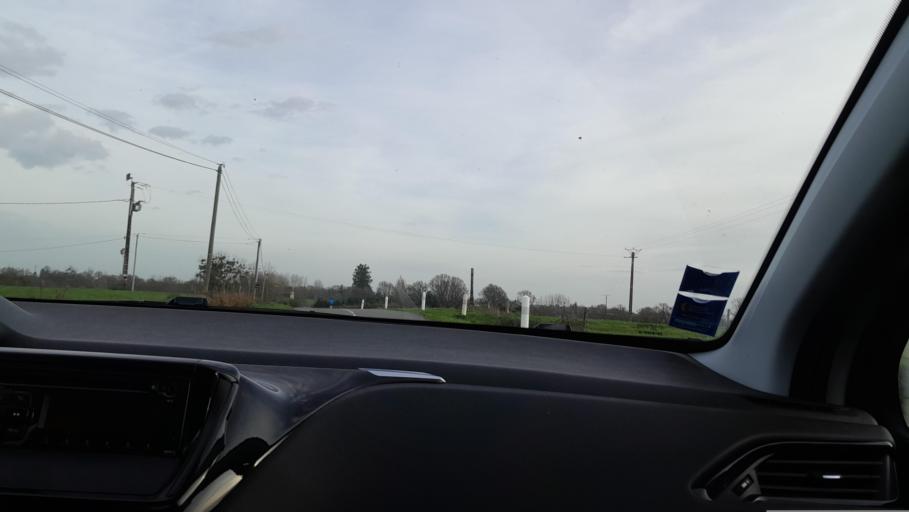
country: FR
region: Brittany
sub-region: Departement d'Ille-et-Vilaine
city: Argentre-du-Plessis
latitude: 47.9655
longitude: -1.1378
